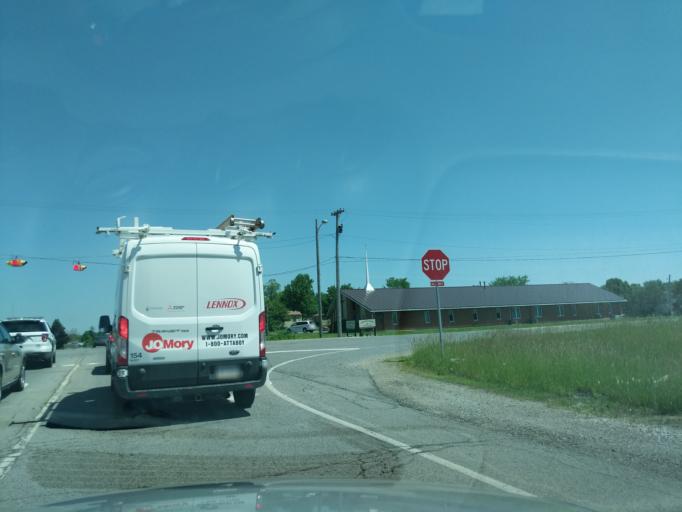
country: US
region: Indiana
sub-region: Whitley County
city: Columbia City
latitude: 41.1698
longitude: -85.4915
